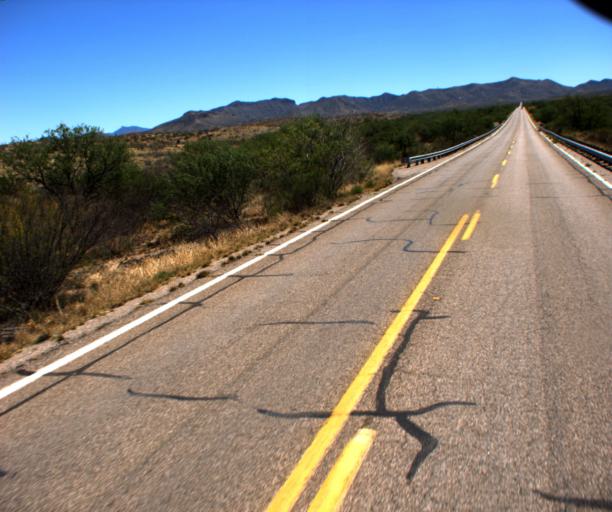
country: US
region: Arizona
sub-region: Pima County
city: Vail
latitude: 31.9710
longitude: -110.6752
